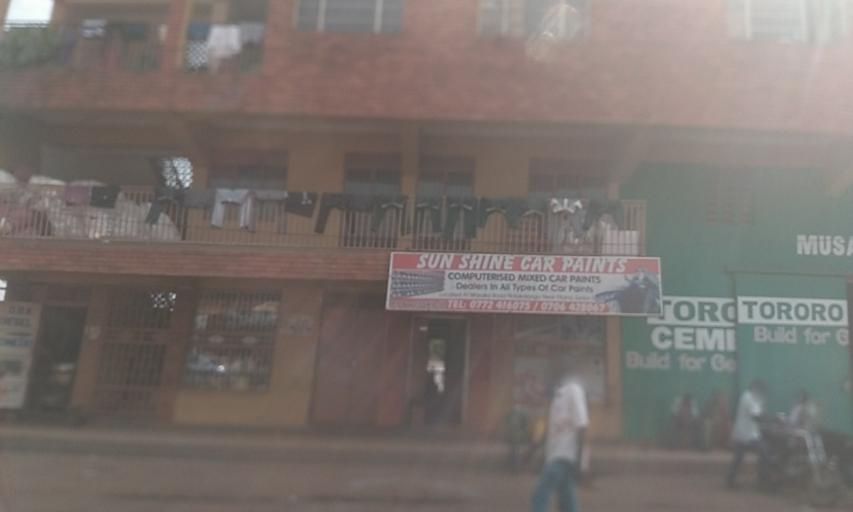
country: UG
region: Central Region
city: Kampala Central Division
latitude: 0.2970
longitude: 32.5408
